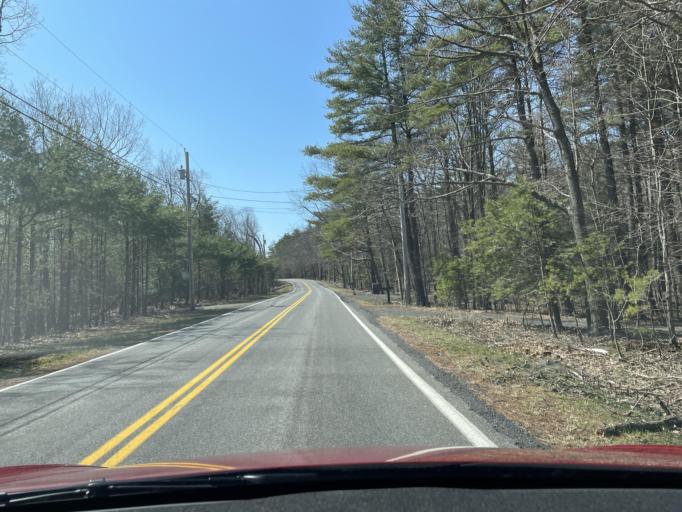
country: US
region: New York
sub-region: Ulster County
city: Zena
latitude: 42.0747
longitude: -74.0698
